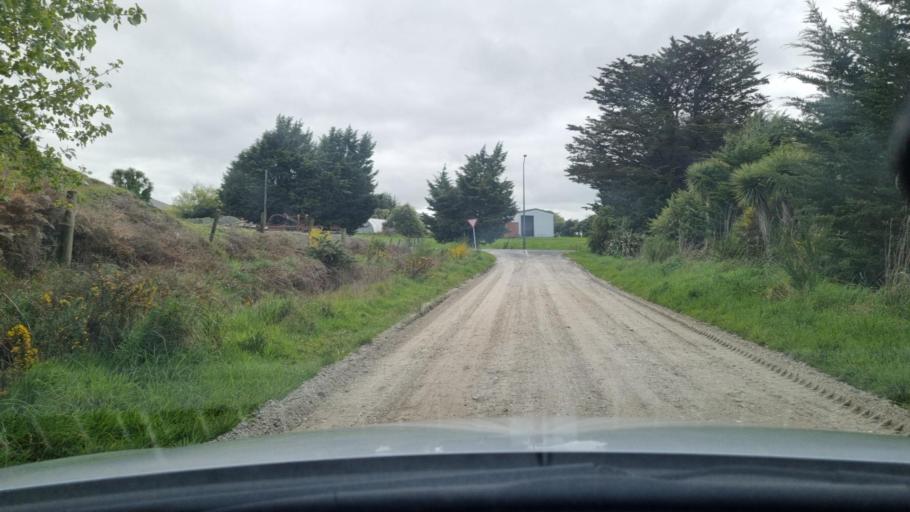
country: NZ
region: Southland
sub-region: Invercargill City
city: Invercargill
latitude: -46.4331
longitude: 168.3896
